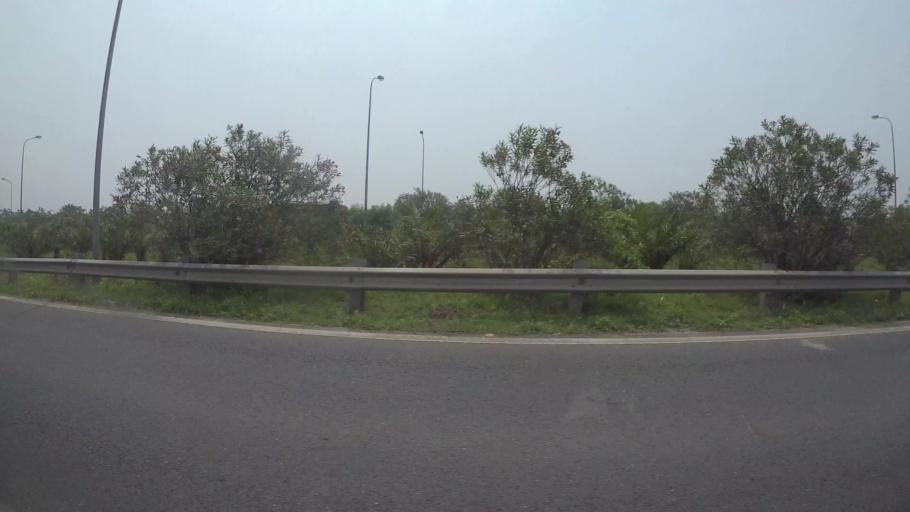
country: VN
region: Ha Noi
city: Quoc Oai
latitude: 20.9940
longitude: 105.5870
